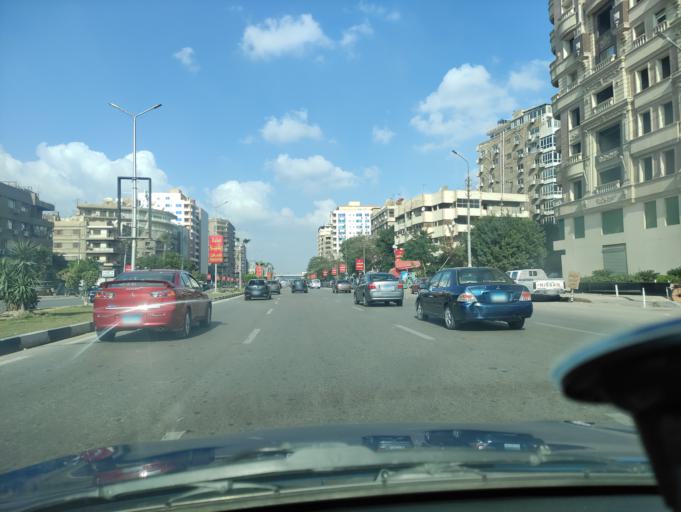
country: EG
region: Muhafazat al Qahirah
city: Cairo
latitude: 30.0869
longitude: 31.3411
